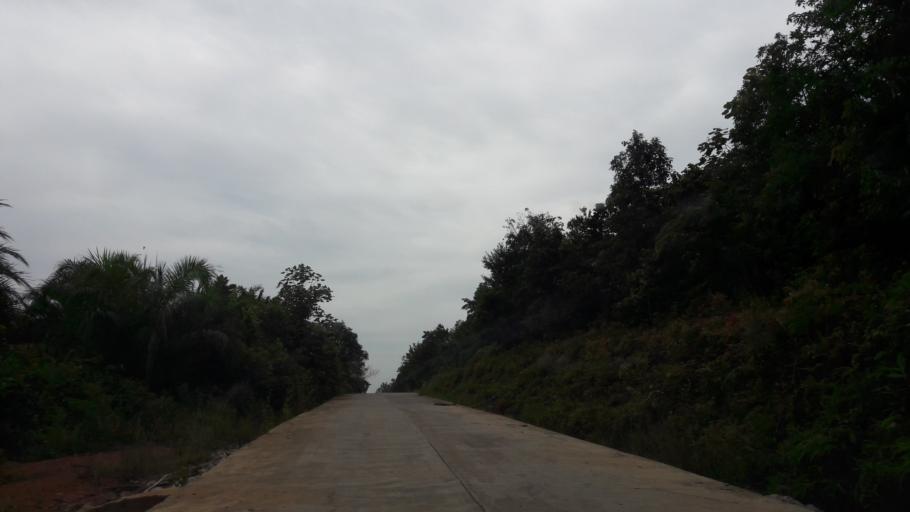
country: ID
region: South Sumatra
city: Gunungmenang
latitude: -3.1961
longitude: 103.8470
